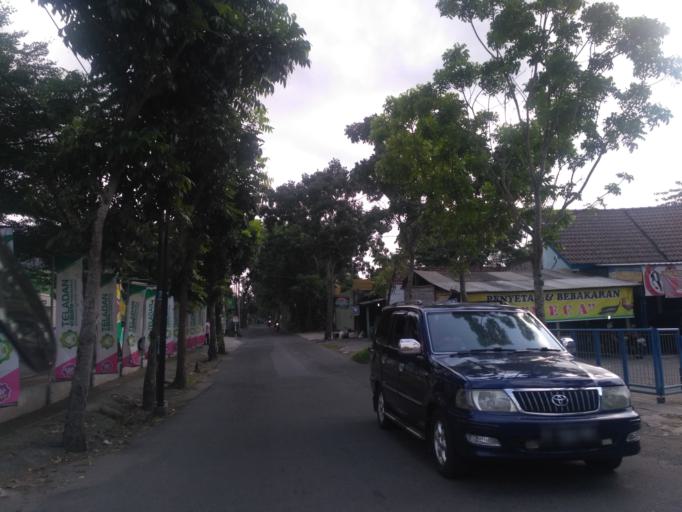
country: ID
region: Daerah Istimewa Yogyakarta
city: Yogyakarta
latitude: -7.7738
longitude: 110.3424
